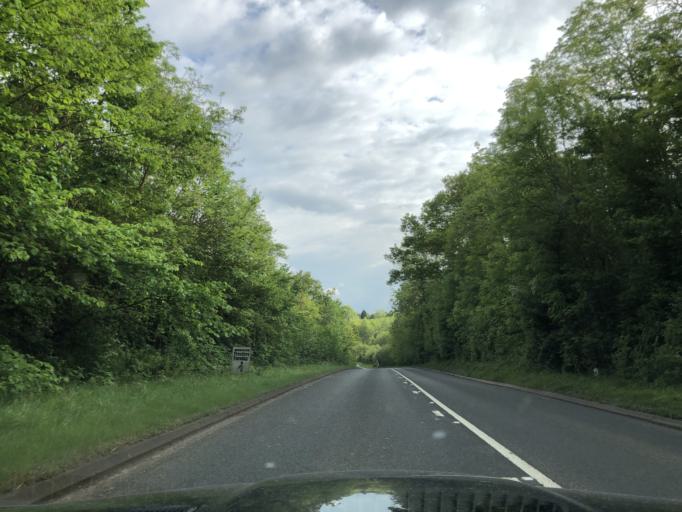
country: GB
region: England
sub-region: Warwickshire
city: Shipston on Stour
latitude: 52.0463
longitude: -1.6678
